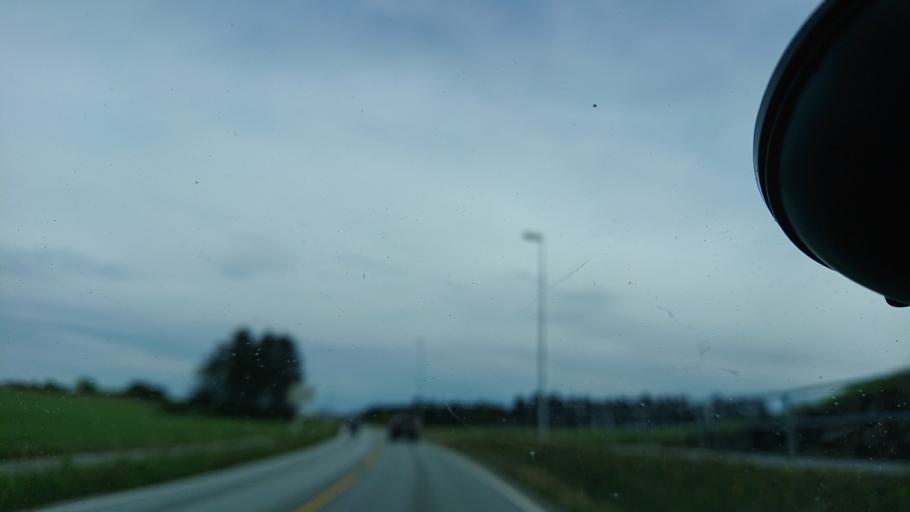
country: NO
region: Rogaland
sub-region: Sola
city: Tananger
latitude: 58.9428
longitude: 5.6005
